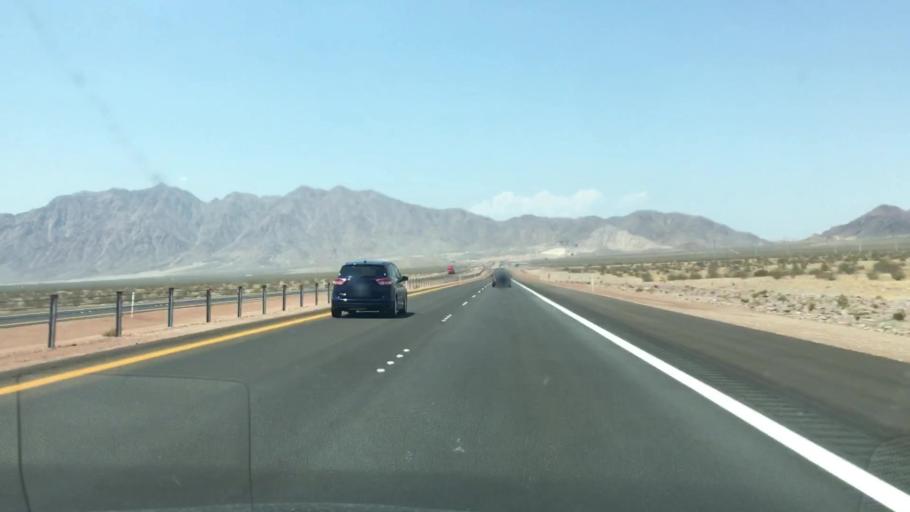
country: US
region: Nevada
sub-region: Clark County
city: Boulder City
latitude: 35.9381
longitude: -114.8707
